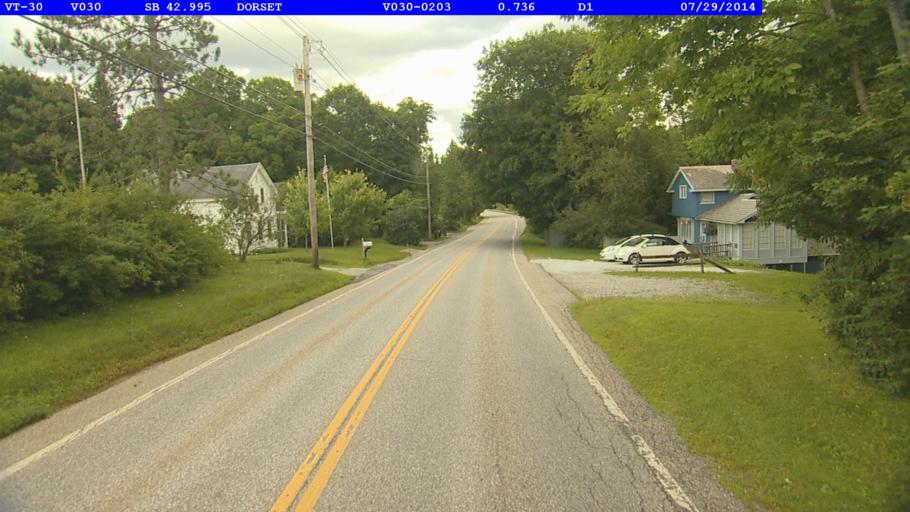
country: US
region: Vermont
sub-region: Bennington County
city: Manchester Center
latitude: 43.2224
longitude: -73.0727
